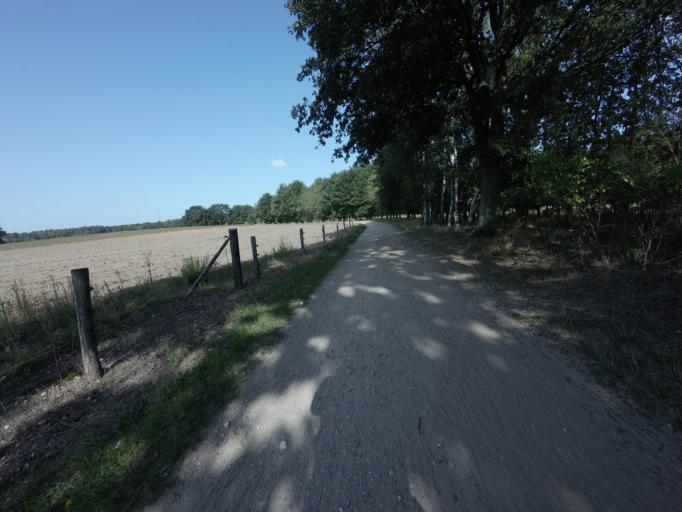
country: NL
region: Limburg
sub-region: Gemeente Roerdalen
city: Herkenbosch
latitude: 51.1704
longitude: 6.0839
